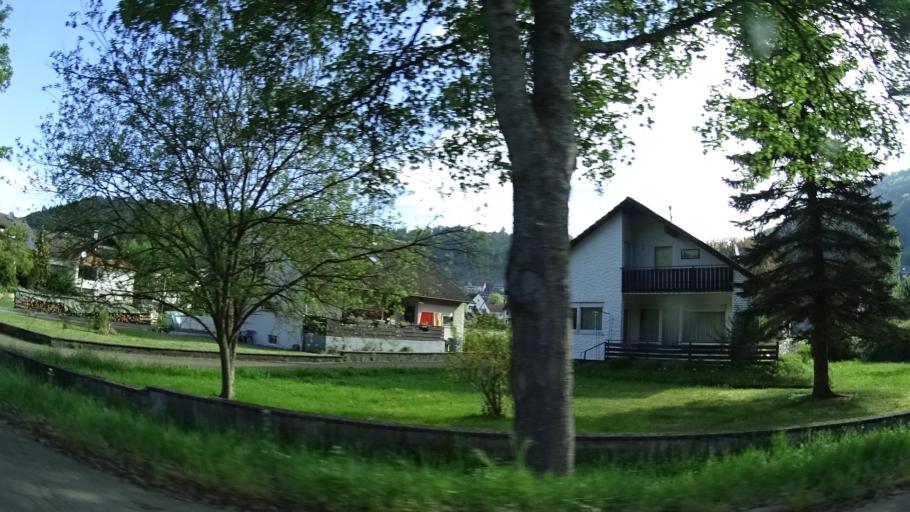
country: DE
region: Baden-Wuerttemberg
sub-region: Tuebingen Region
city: Haigerloch
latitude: 48.4010
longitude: 8.7754
